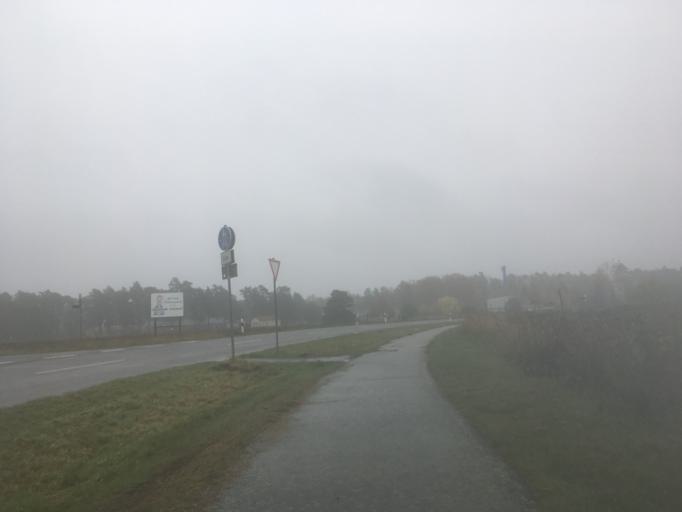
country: DE
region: Brandenburg
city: Schlepzig
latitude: 52.0218
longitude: 14.0101
